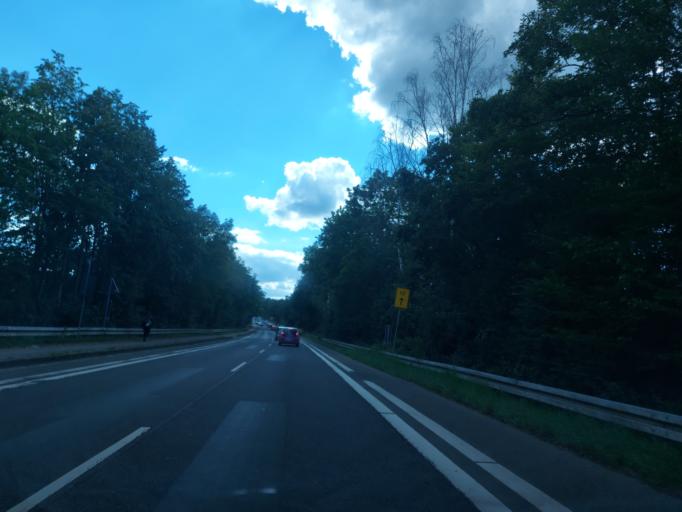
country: DE
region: Lower Saxony
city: Georgsmarienhutte
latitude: 52.2313
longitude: 8.0185
